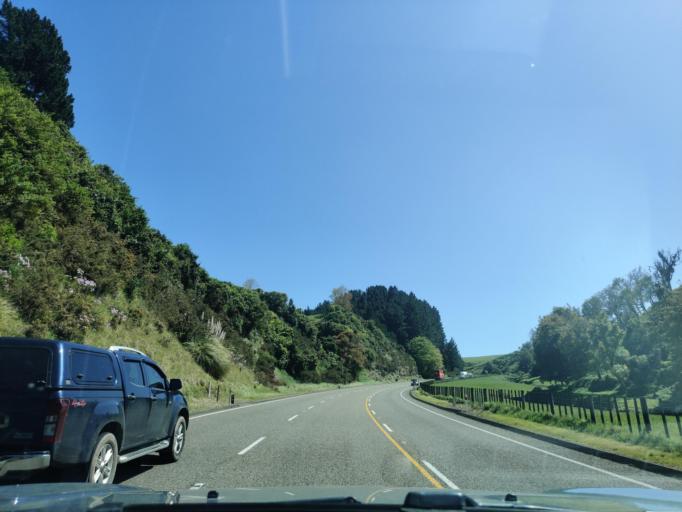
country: NZ
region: Manawatu-Wanganui
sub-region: Wanganui District
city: Wanganui
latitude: -39.8302
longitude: 174.8833
